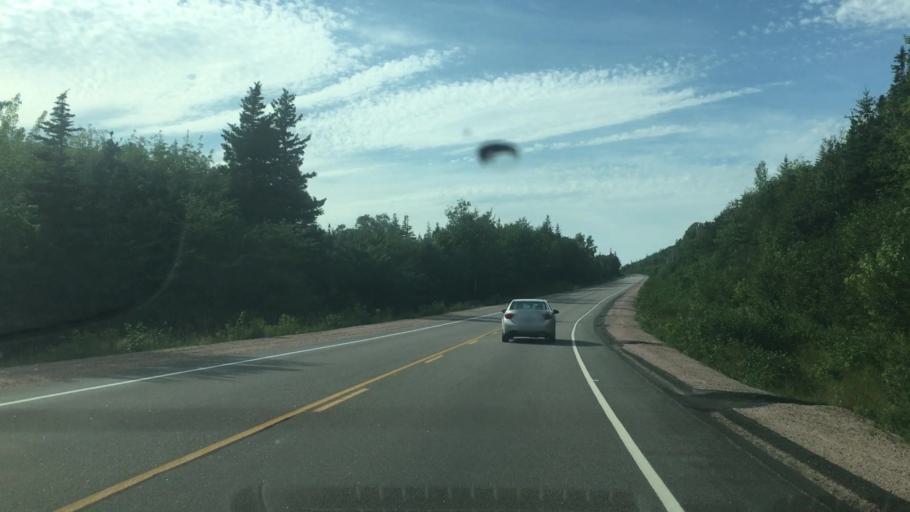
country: CA
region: Nova Scotia
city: Sydney Mines
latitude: 46.8150
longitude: -60.3408
